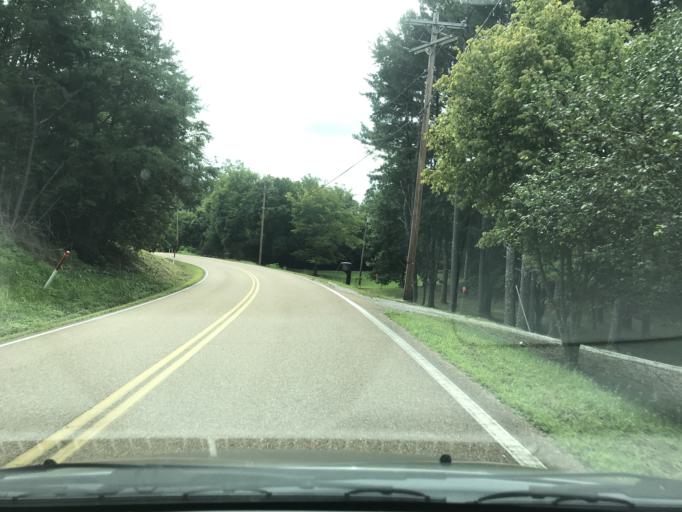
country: US
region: Tennessee
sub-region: Hamilton County
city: Lakesite
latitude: 35.2048
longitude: -85.0726
